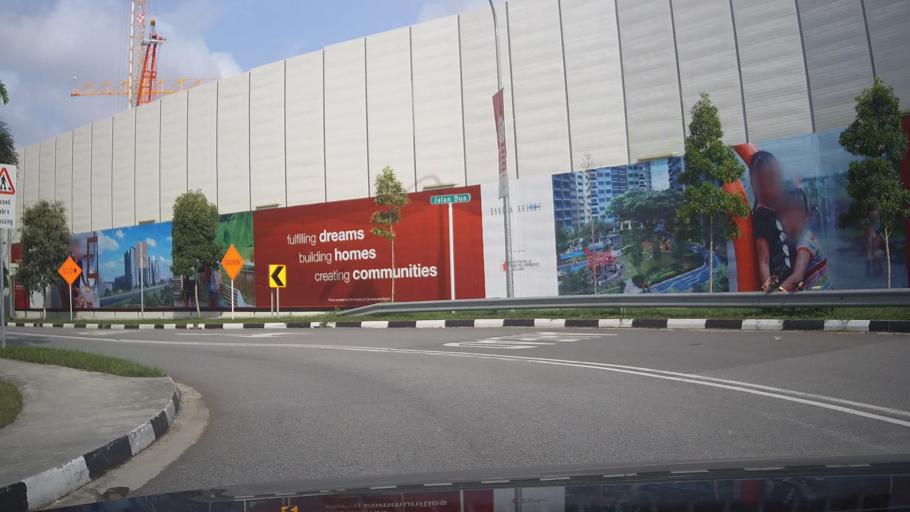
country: SG
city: Singapore
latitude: 1.3090
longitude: 103.8888
